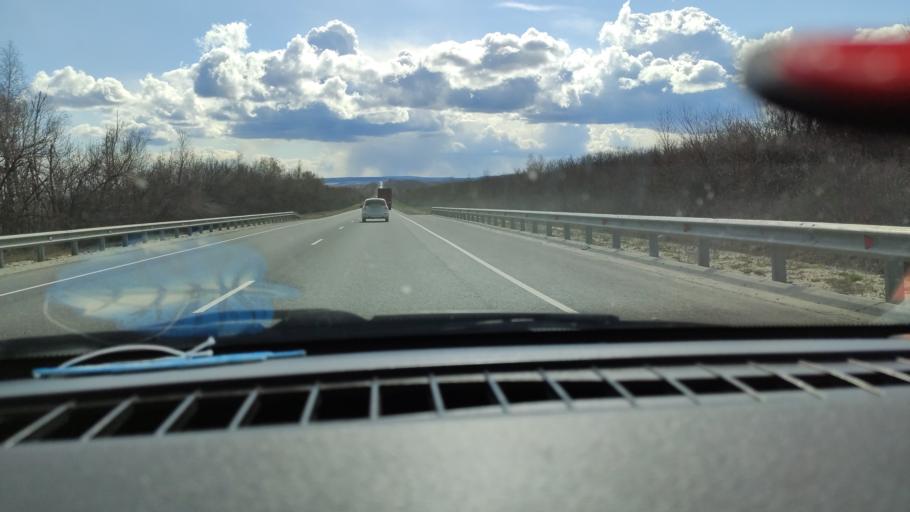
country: RU
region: Saratov
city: Khvalynsk
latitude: 52.6138
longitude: 48.1629
